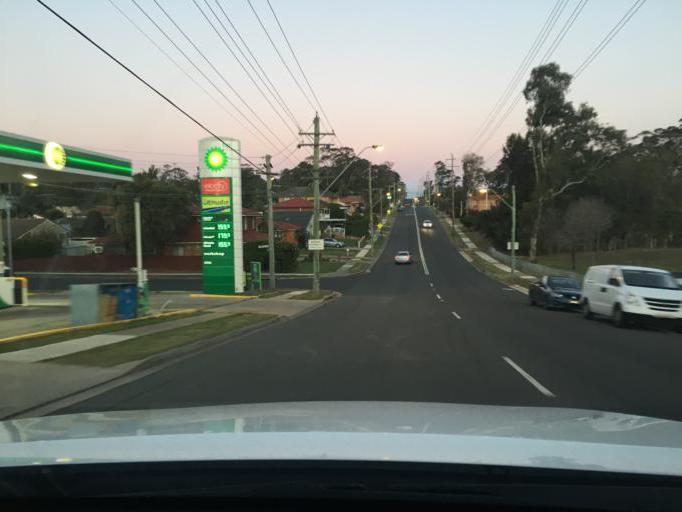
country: AU
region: New South Wales
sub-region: Holroyd
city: Girraween
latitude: -33.8280
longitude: 150.9374
